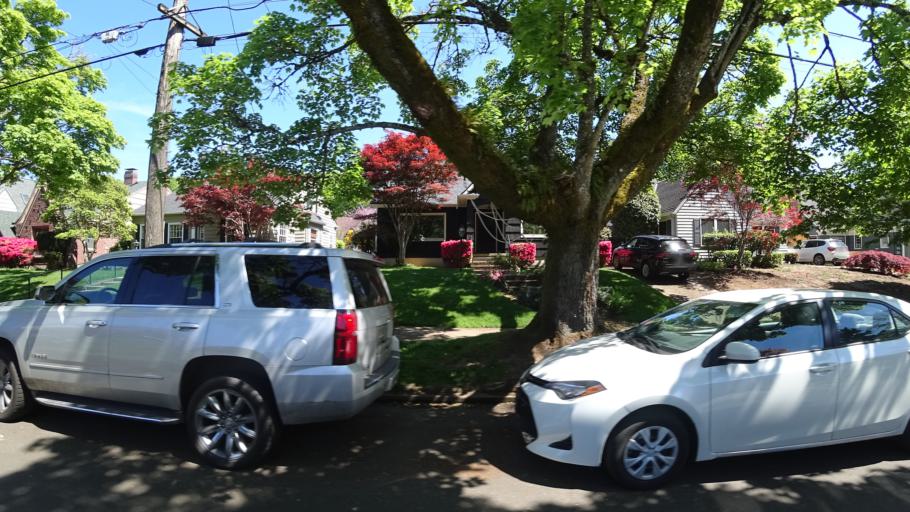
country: US
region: Oregon
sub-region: Clackamas County
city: Milwaukie
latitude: 45.4723
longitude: -122.6304
